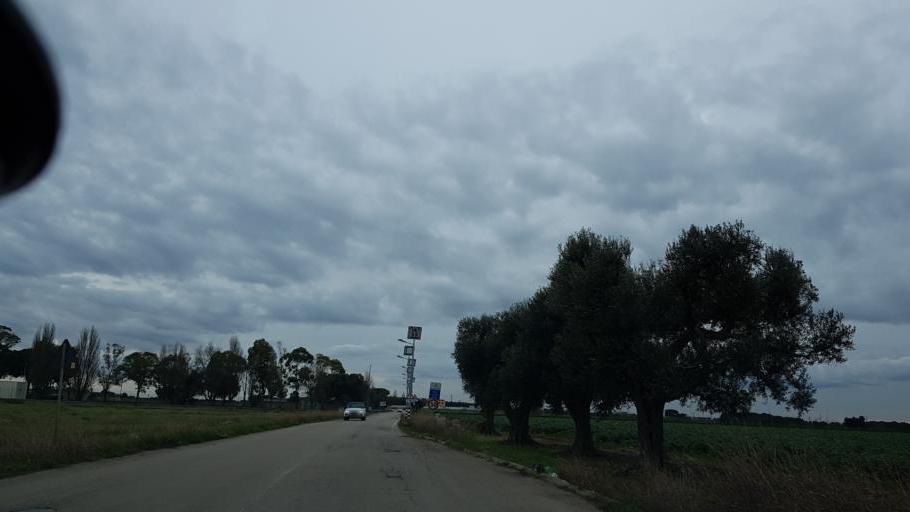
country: IT
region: Apulia
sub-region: Provincia di Brindisi
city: La Rosa
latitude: 40.6160
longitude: 17.9449
